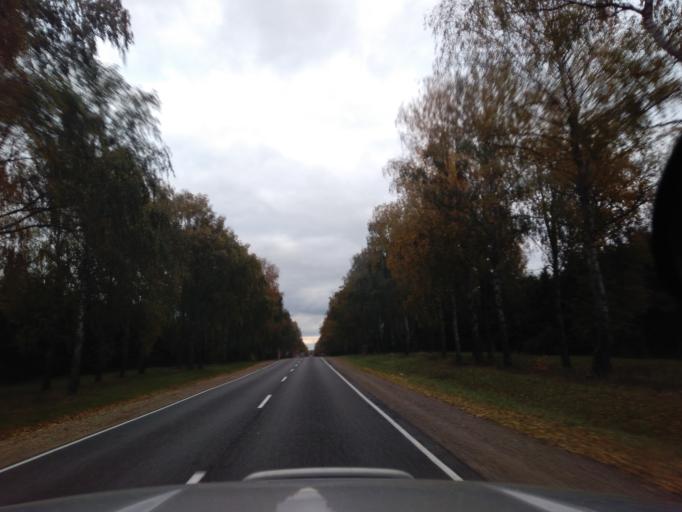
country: BY
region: Minsk
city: Slutsk
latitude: 53.2196
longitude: 27.4594
